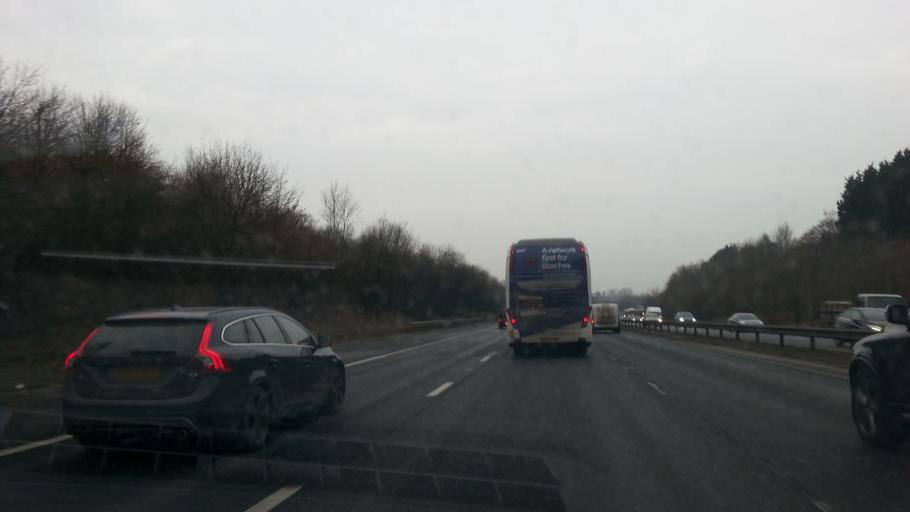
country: GB
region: England
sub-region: Hertfordshire
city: Sawbridgeworth
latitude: 51.8033
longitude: 0.1759
